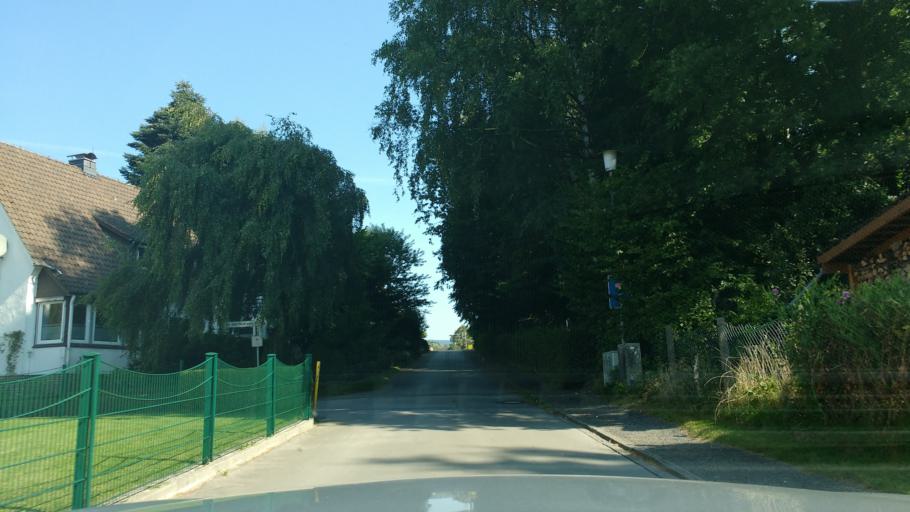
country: DE
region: North Rhine-Westphalia
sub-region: Regierungsbezirk Detmold
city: Dorentrup
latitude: 52.0397
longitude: 9.0066
